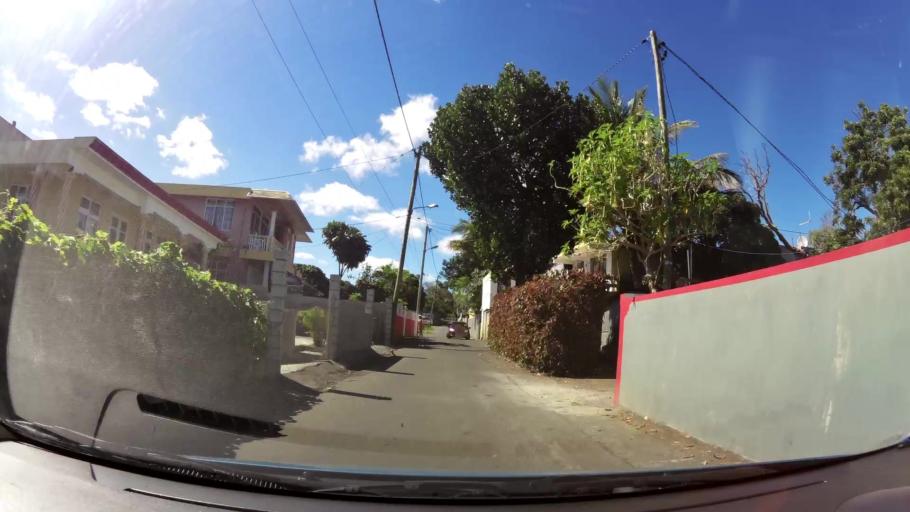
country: MU
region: Plaines Wilhems
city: Vacoas
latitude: -20.3097
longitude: 57.4733
